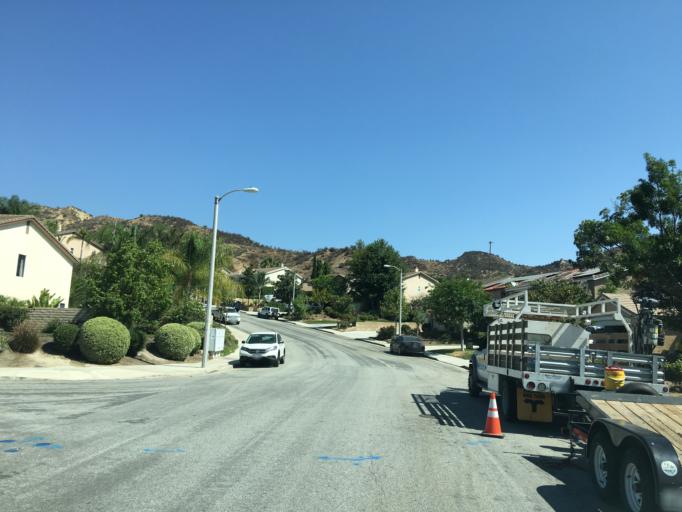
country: US
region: California
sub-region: Los Angeles County
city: Castaic
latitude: 34.4729
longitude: -118.6333
